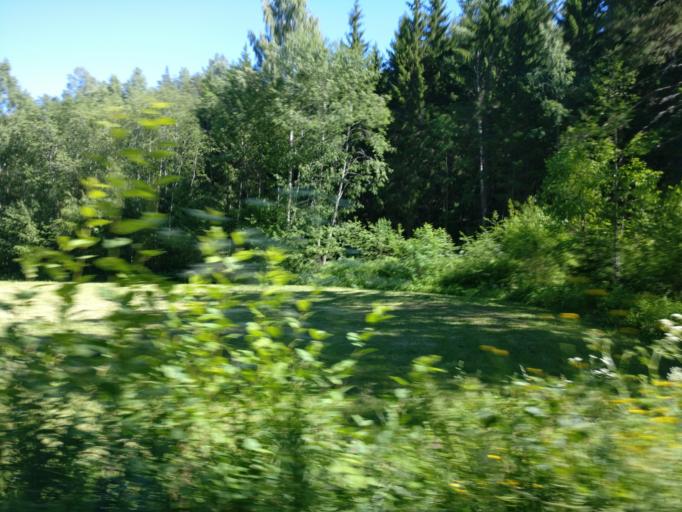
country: FI
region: Southern Savonia
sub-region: Savonlinna
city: Rantasalmi
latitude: 62.1662
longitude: 28.2533
